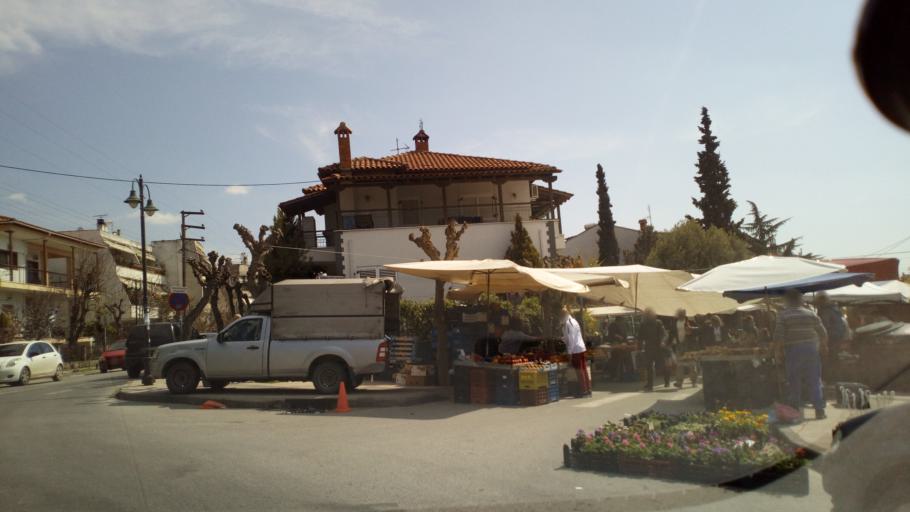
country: GR
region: Central Macedonia
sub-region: Nomos Thessalonikis
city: Thermi
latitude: 40.5503
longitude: 23.0212
